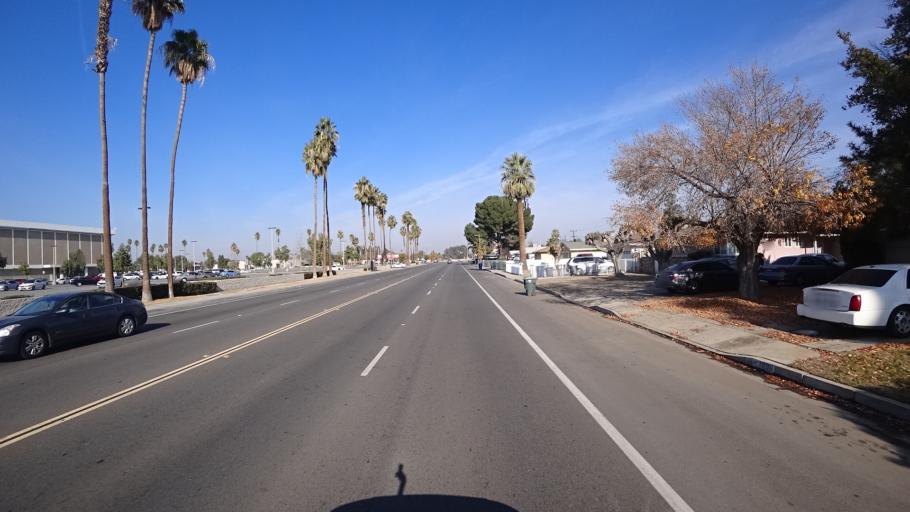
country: US
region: California
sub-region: Kern County
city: Bakersfield
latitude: 35.3376
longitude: -119.0300
